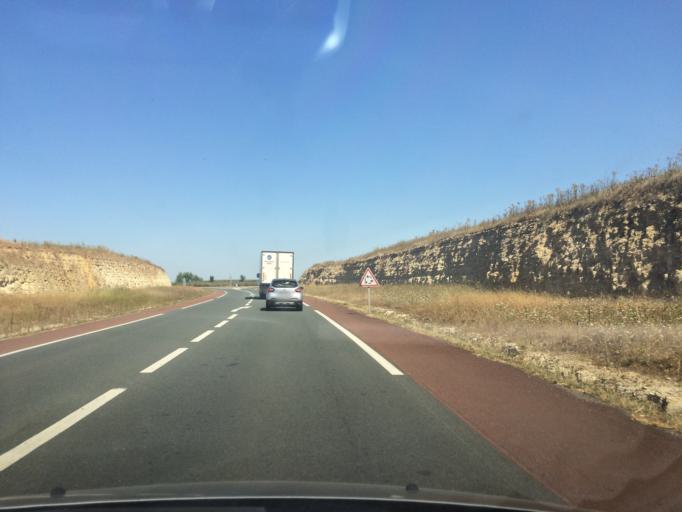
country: FR
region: Poitou-Charentes
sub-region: Departement de la Charente-Maritime
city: Esnandes
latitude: 46.2407
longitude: -1.0783
